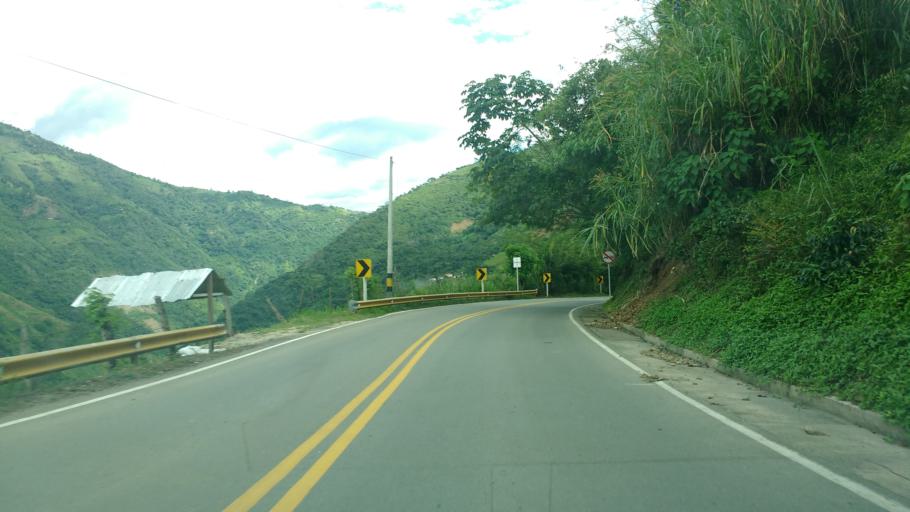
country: CO
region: Antioquia
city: Titiribi
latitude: 6.0637
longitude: -75.7497
